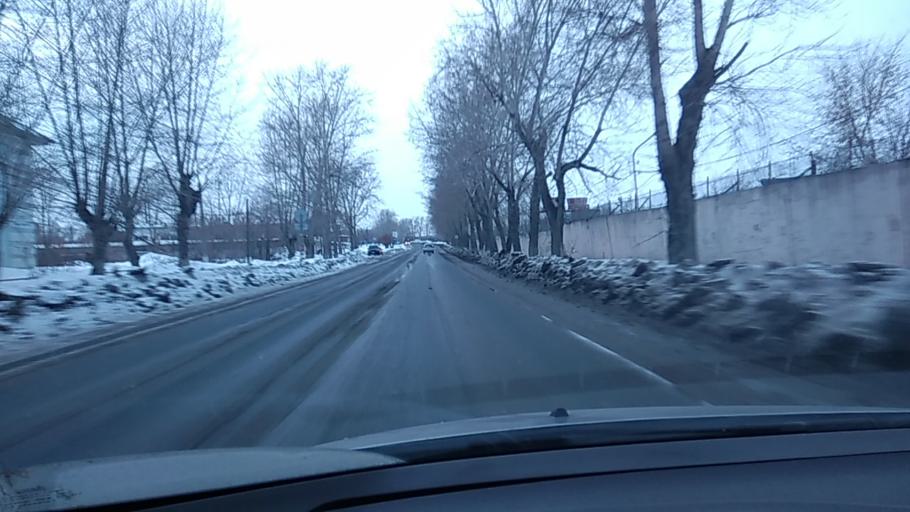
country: RU
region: Sverdlovsk
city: Martyush
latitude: 56.4465
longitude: 61.8163
